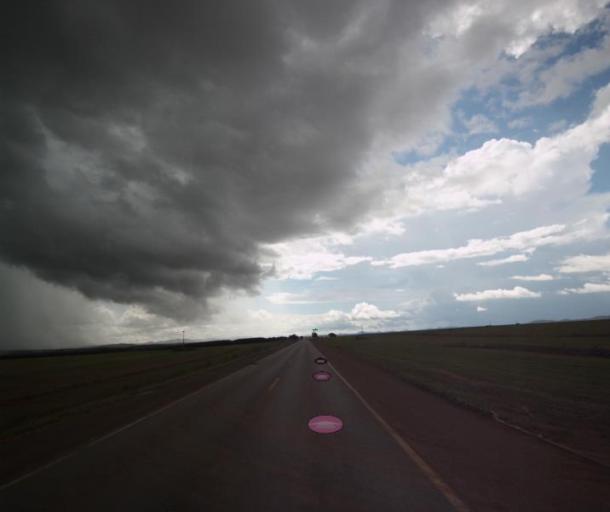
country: BR
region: Goias
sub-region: Uruacu
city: Uruacu
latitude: -14.6442
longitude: -49.1709
